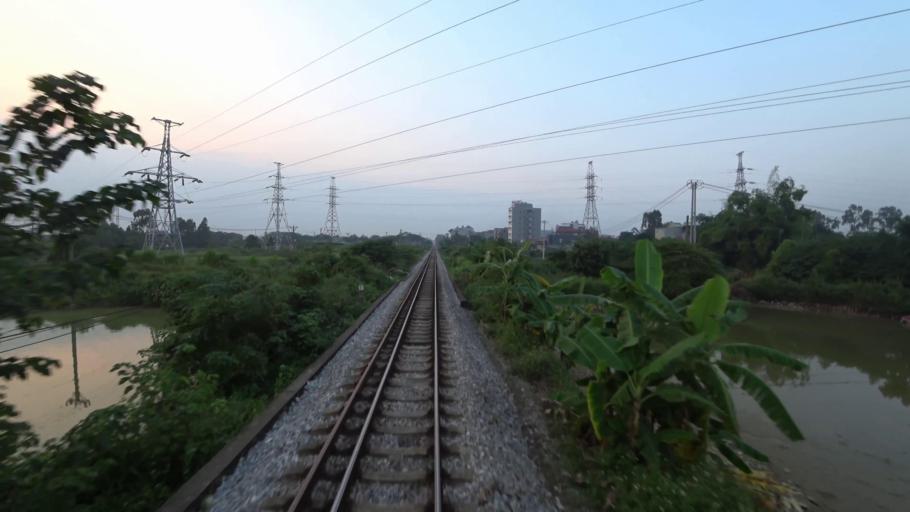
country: VN
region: Ha Noi
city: Dong Anh
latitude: 21.1474
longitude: 105.8590
